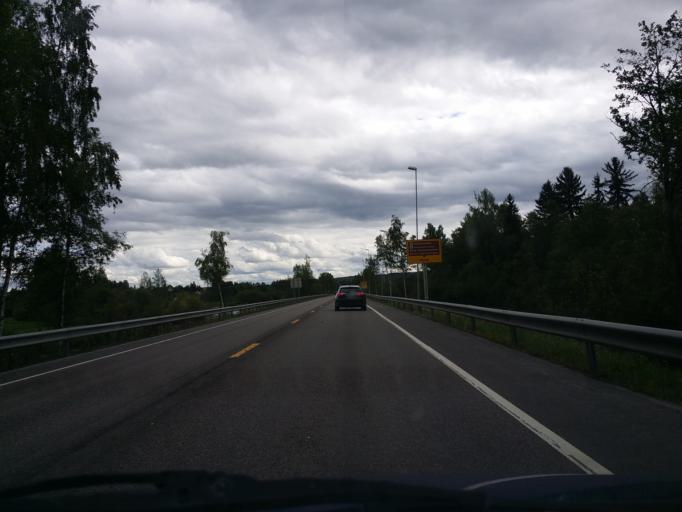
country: NO
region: Hedmark
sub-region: Hamar
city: Hamar
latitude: 60.8086
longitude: 11.1066
